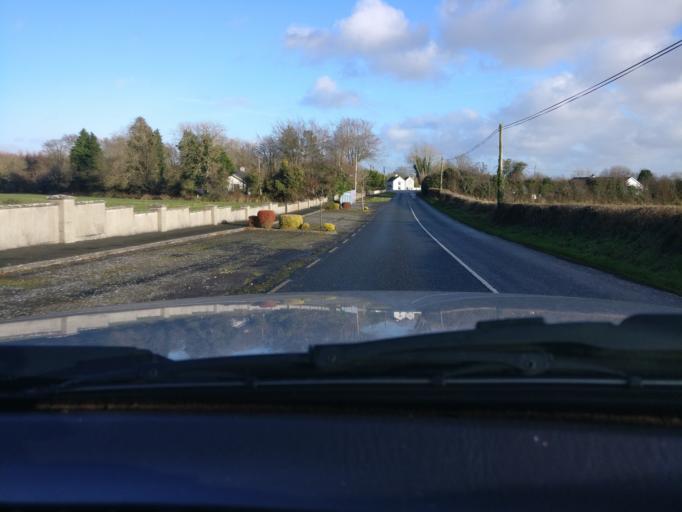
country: IE
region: Leinster
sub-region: An Iarmhi
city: Kilbeggan
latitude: 53.4722
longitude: -7.4621
